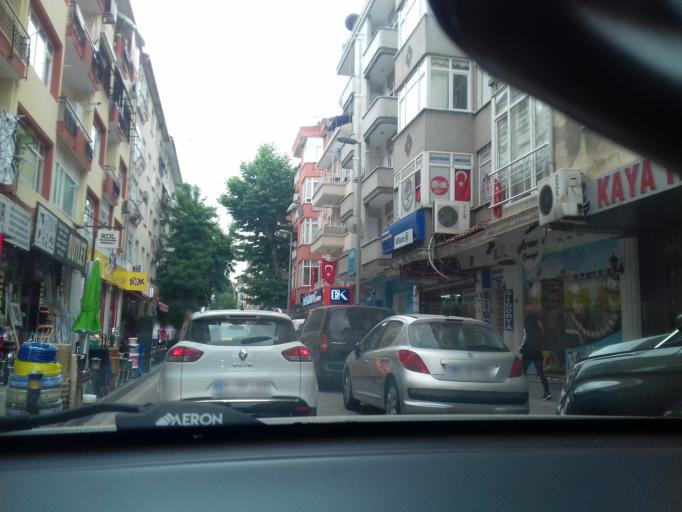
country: TR
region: Istanbul
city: Pendik
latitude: 40.8798
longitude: 29.2344
